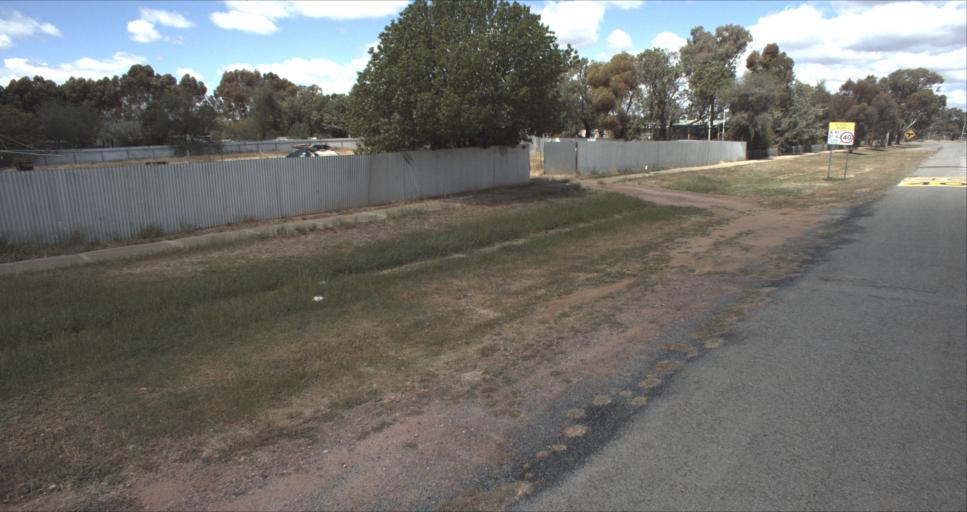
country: AU
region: New South Wales
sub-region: Murrumbidgee Shire
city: Darlington Point
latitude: -34.5179
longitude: 146.1805
